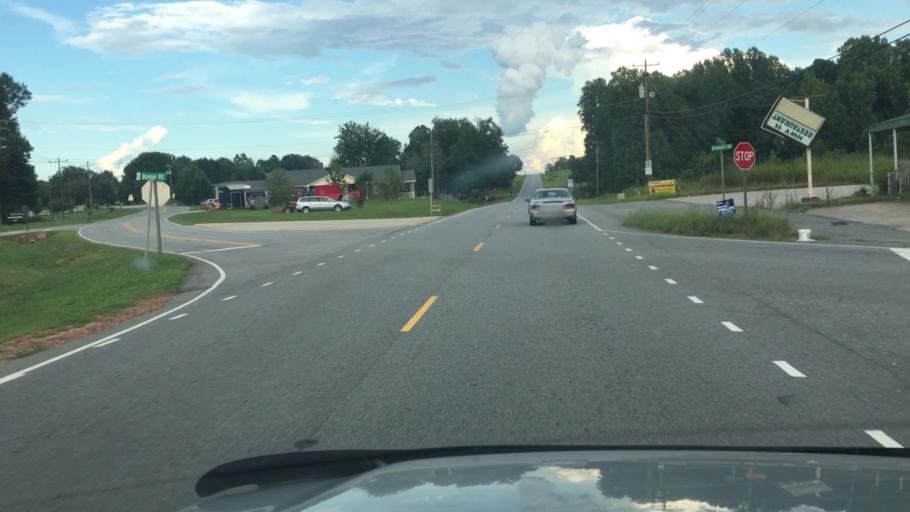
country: US
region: South Carolina
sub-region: Spartanburg County
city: Mayo
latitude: 35.1272
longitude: -81.7827
